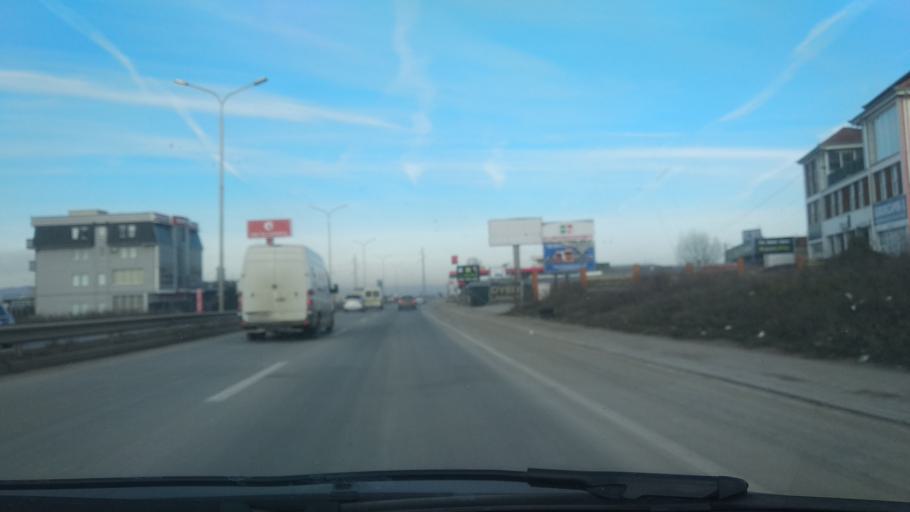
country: XK
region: Pristina
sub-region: Kosovo Polje
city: Kosovo Polje
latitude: 42.6609
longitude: 21.1322
